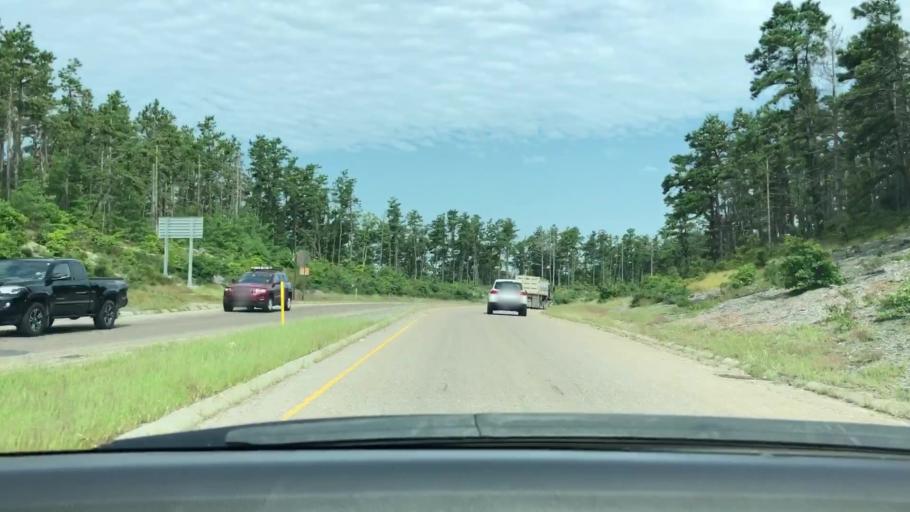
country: US
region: Massachusetts
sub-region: Plymouth County
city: White Island Shores
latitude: 41.8729
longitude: -70.6036
